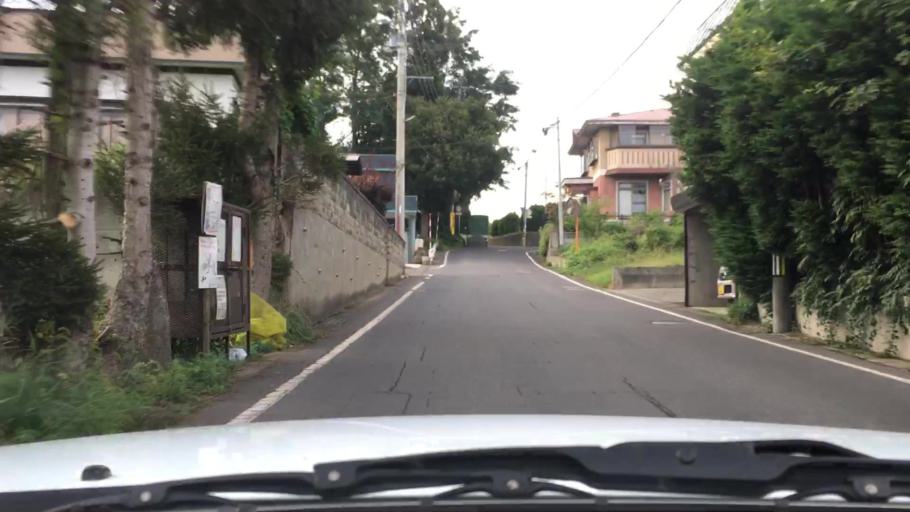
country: JP
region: Aomori
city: Hirosaki
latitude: 40.5782
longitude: 140.4568
